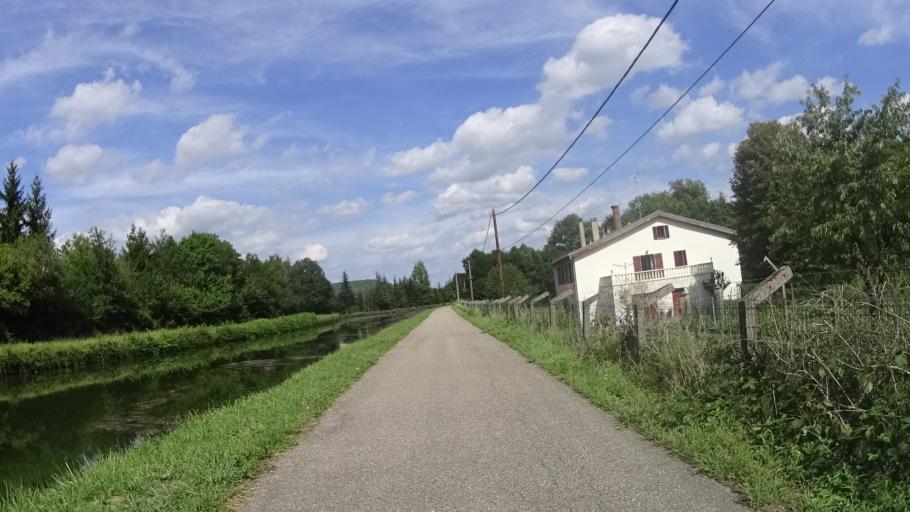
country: FR
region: Lorraine
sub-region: Departement de Meurthe-et-Moselle
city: Ecrouves
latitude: 48.6767
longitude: 5.8422
